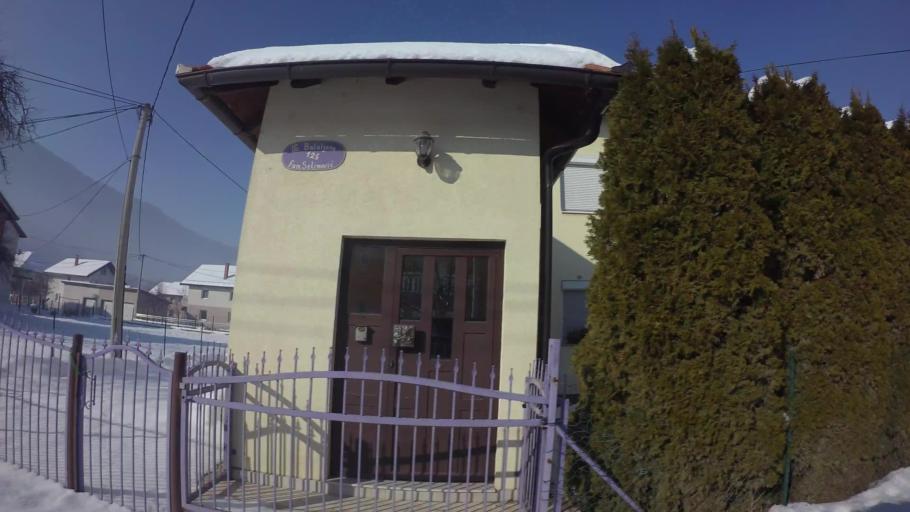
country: BA
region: Federation of Bosnia and Herzegovina
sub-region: Kanton Sarajevo
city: Sarajevo
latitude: 43.8043
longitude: 18.3025
